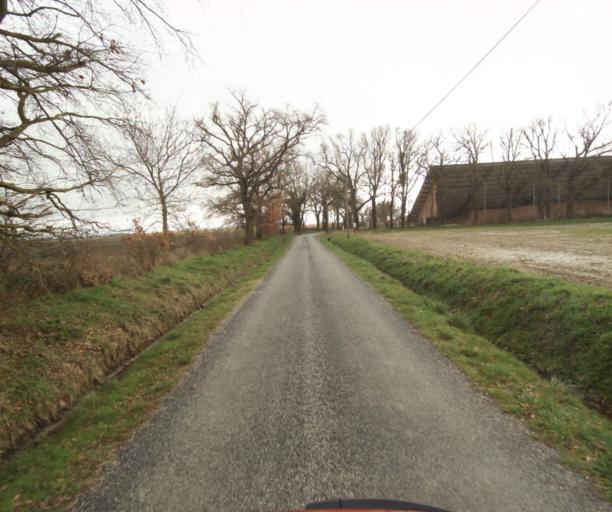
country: FR
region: Midi-Pyrenees
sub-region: Departement de l'Ariege
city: Mazeres
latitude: 43.2000
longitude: 1.6717
